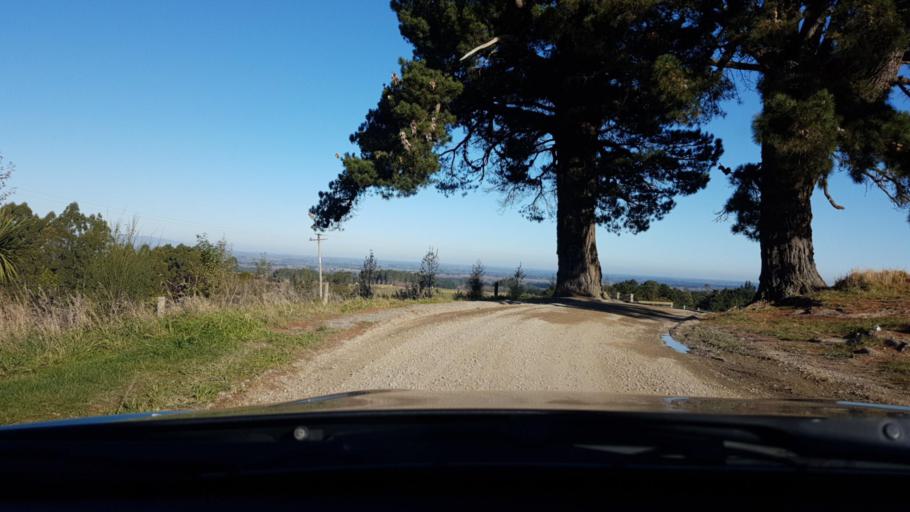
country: NZ
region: Canterbury
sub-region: Waimakariri District
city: Woodend
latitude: -43.2447
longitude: 172.5774
